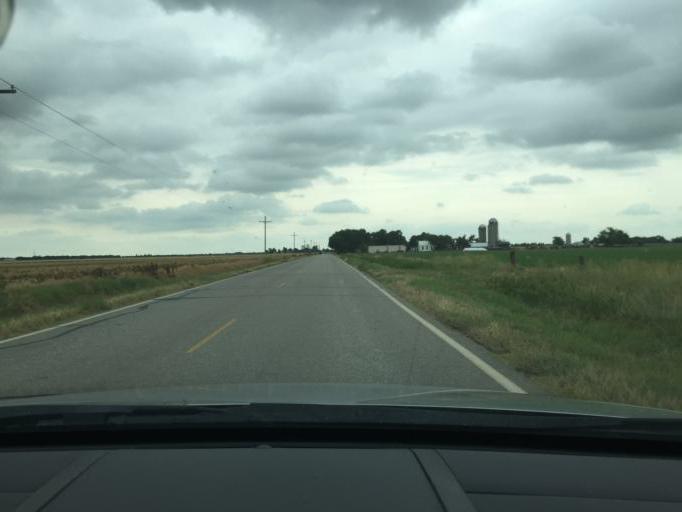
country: US
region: Kansas
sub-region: Reno County
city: South Hutchinson
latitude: 37.9773
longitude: -98.0138
